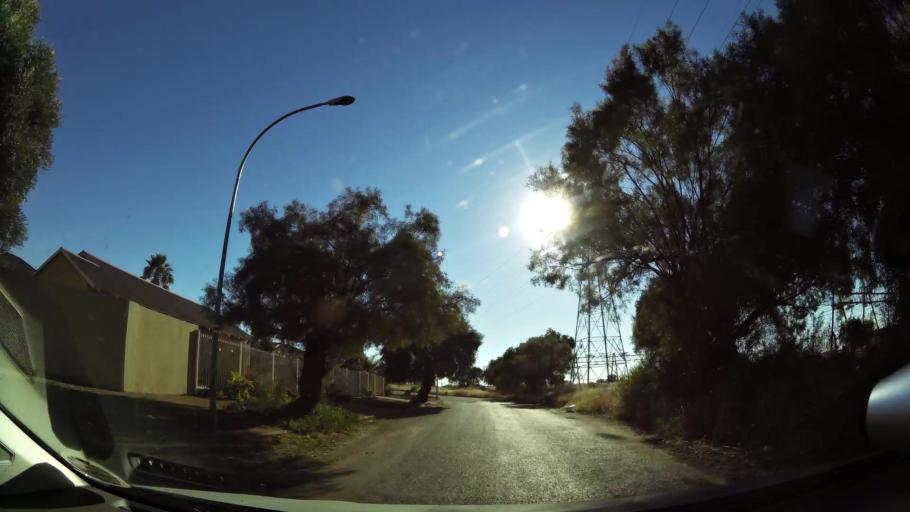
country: ZA
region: Northern Cape
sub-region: Frances Baard District Municipality
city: Kimberley
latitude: -28.7540
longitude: 24.7893
